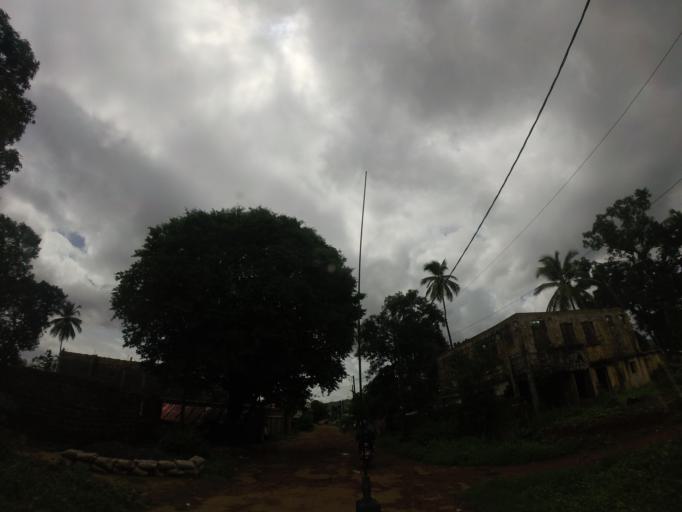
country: SL
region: Western Area
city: Hastings
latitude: 8.3801
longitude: -13.1366
